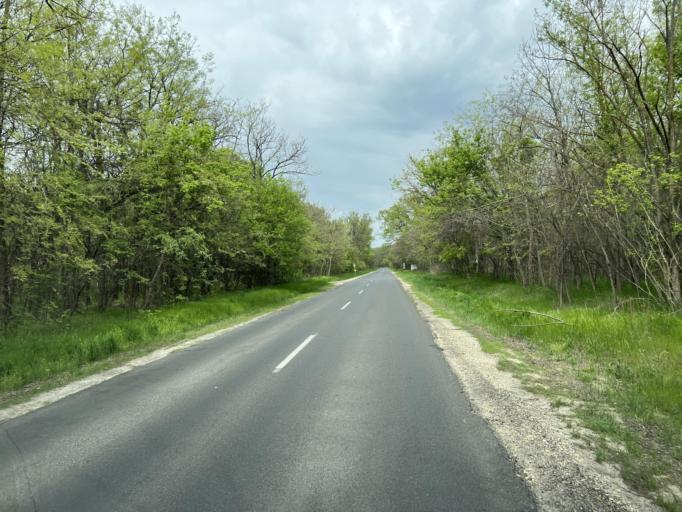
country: HU
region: Pest
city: Cegled
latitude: 47.1487
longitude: 19.8659
